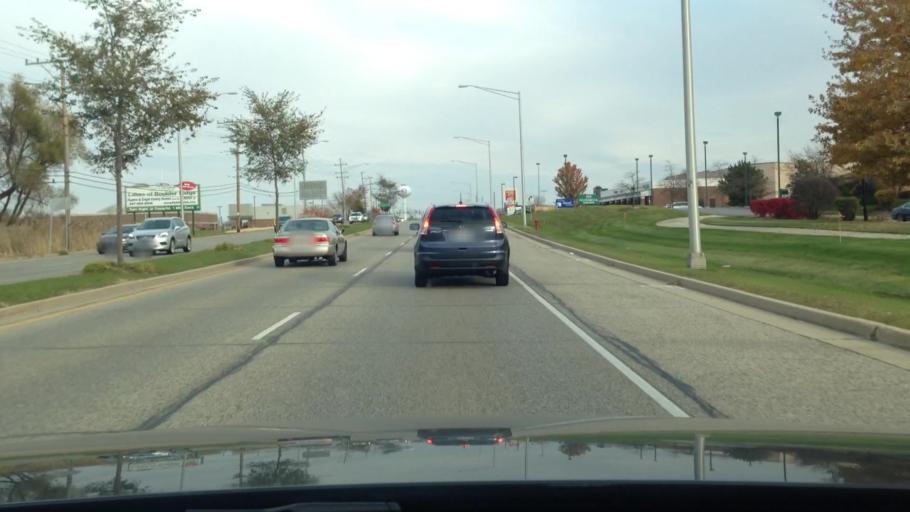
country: US
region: Illinois
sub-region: McHenry County
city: Lake in the Hills
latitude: 42.1756
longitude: -88.3409
